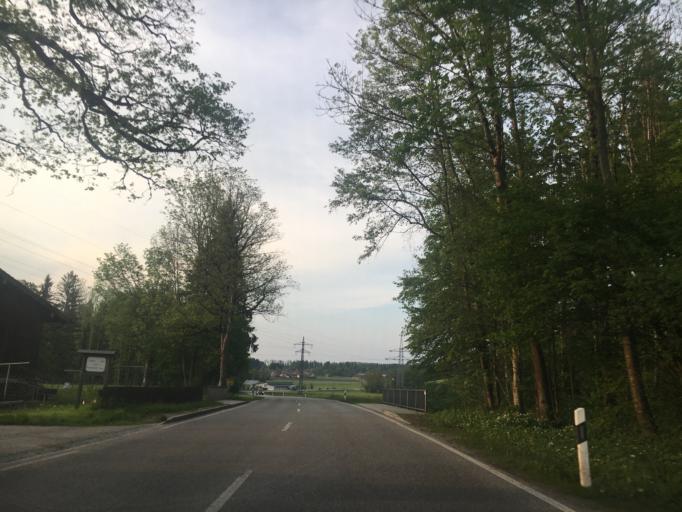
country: DE
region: Bavaria
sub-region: Upper Bavaria
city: Benediktbeuern
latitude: 47.6793
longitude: 11.4003
